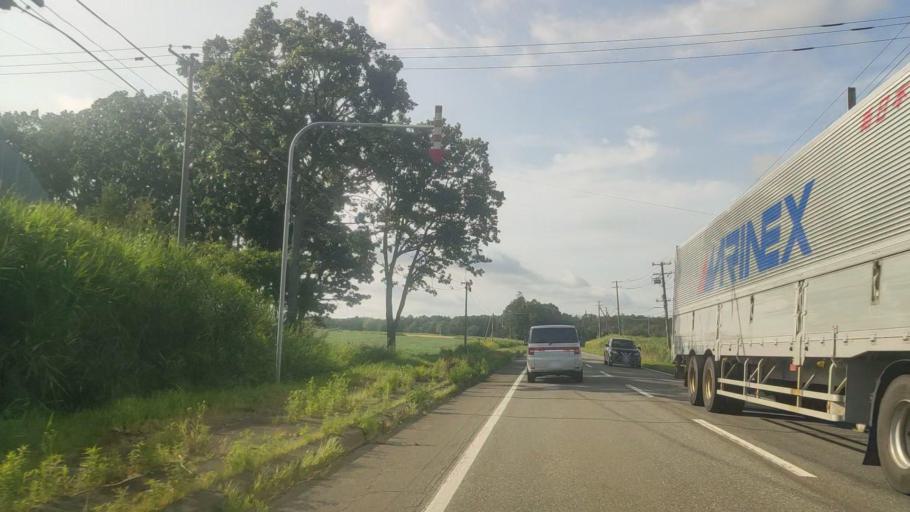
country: JP
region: Hokkaido
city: Chitose
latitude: 42.8009
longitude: 141.8352
